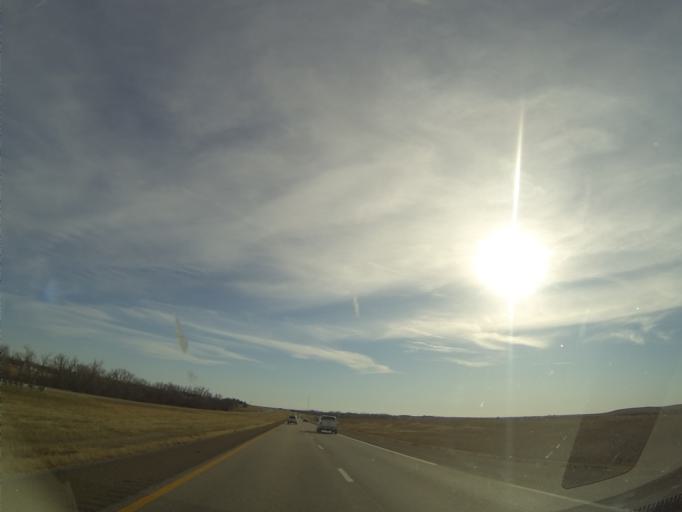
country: US
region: Kansas
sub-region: Saline County
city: Salina
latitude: 38.9717
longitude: -97.6403
